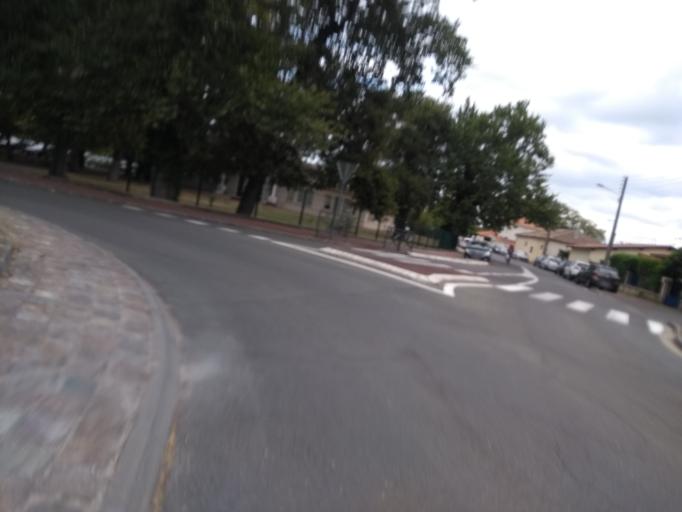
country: FR
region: Aquitaine
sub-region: Departement de la Gironde
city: Merignac
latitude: 44.8249
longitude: -0.6455
